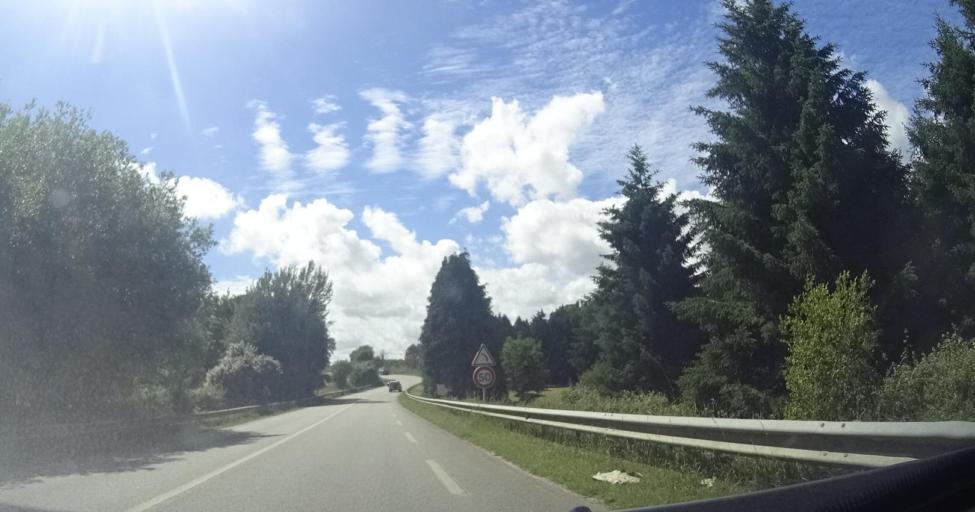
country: FR
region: Brittany
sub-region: Departement du Morbihan
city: Trefflean
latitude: 47.6960
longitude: -2.6260
